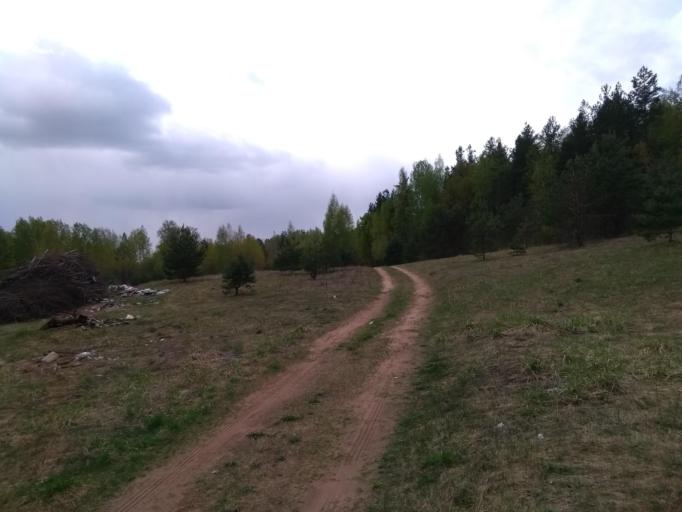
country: RU
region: Pskov
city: Loknya
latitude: 56.6776
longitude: 30.1814
